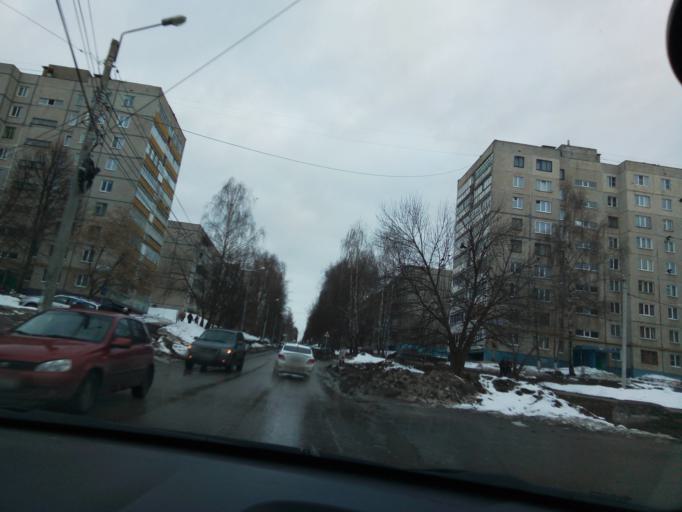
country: RU
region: Chuvashia
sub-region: Cheboksarskiy Rayon
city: Cheboksary
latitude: 56.1482
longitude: 47.1780
